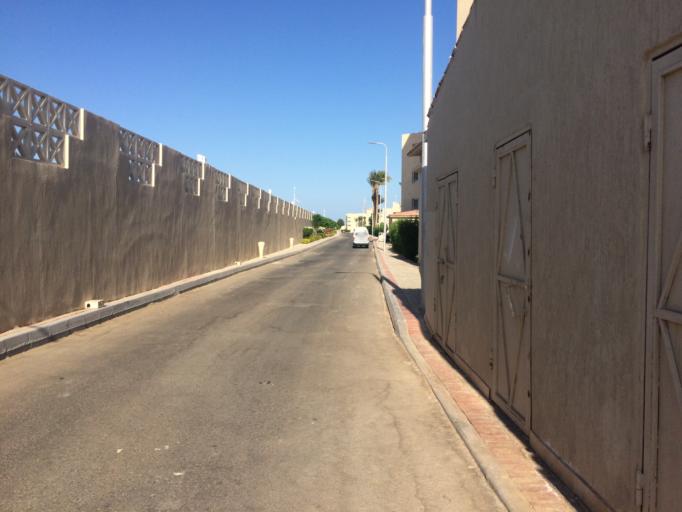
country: EG
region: Red Sea
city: Hurghada
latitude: 27.1231
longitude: 33.8243
